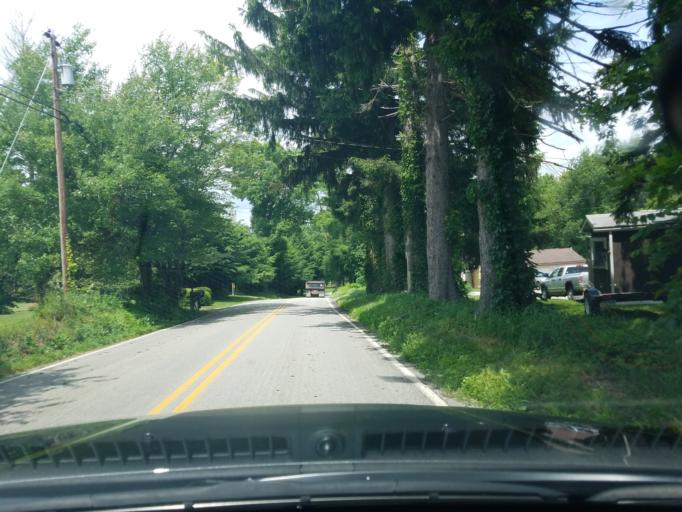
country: US
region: Pennsylvania
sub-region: Fayette County
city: Bear Rocks
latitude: 40.1531
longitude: -79.3402
